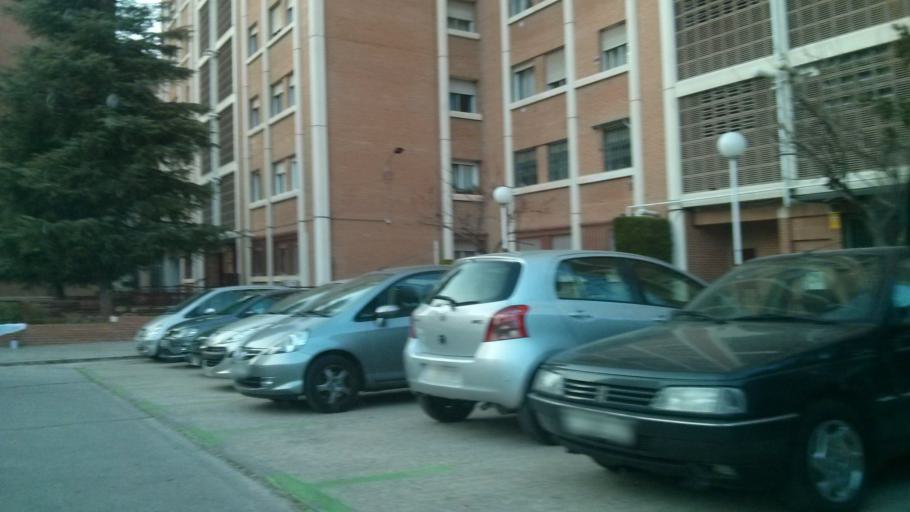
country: ES
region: Madrid
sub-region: Provincia de Madrid
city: Tetuan de las Victorias
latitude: 40.4757
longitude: -3.6978
